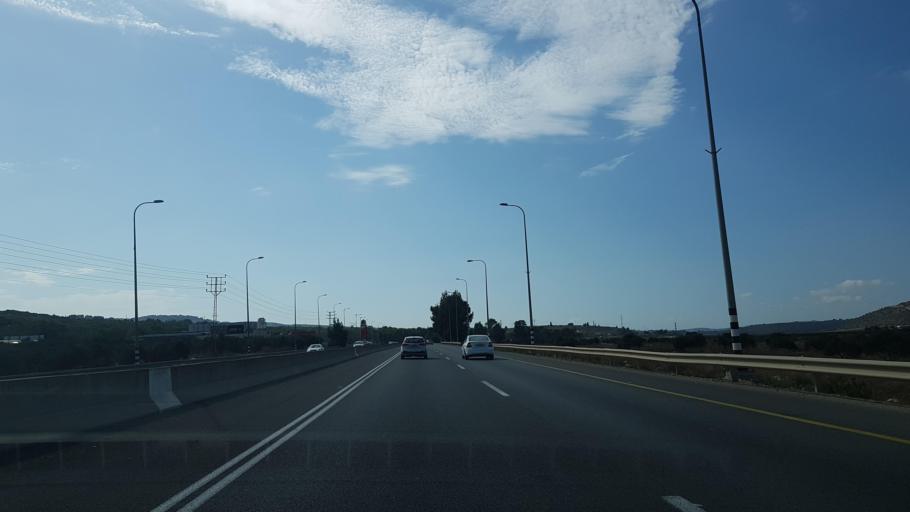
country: IL
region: Northern District
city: Kafr Kanna
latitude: 32.7610
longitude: 35.3629
